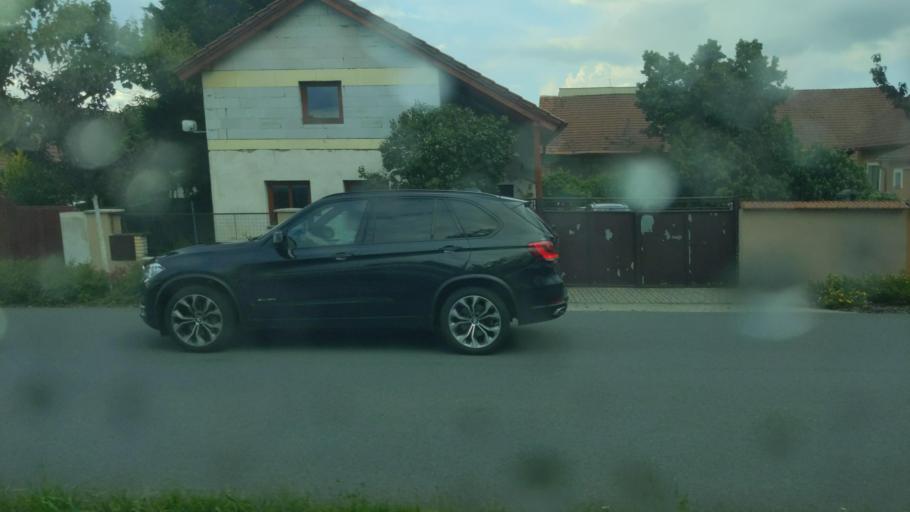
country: CZ
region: Central Bohemia
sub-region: Okres Nymburk
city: Sadska
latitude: 50.1260
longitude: 14.9613
